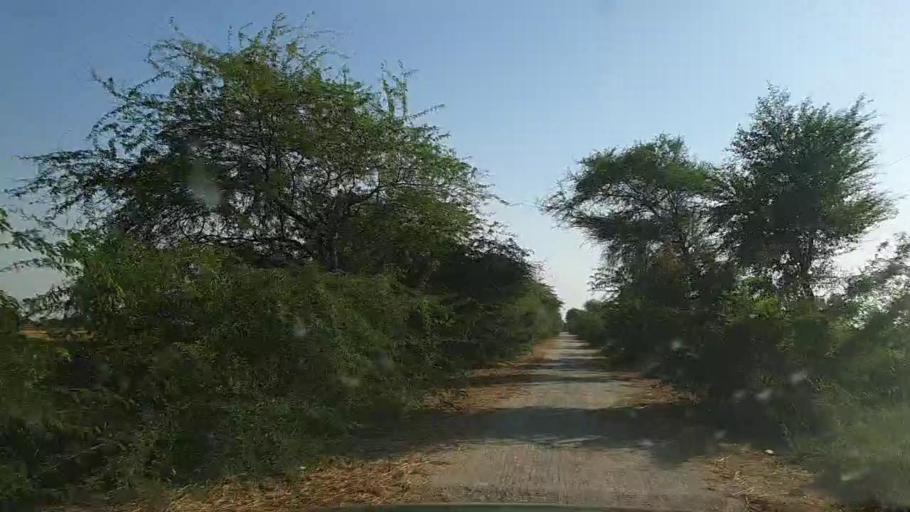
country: PK
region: Sindh
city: Daro Mehar
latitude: 24.6493
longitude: 68.0750
